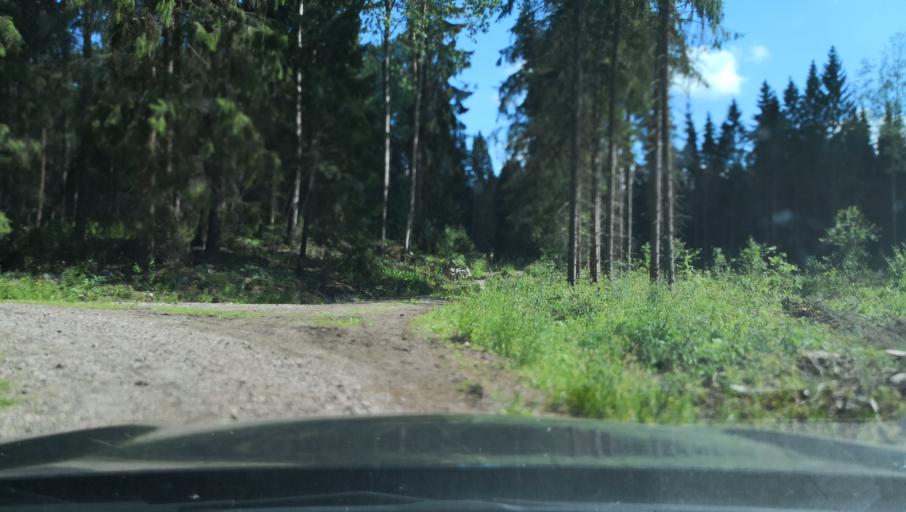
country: SE
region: Vaestmanland
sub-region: Kungsors Kommun
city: Kungsoer
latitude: 59.3399
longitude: 16.0624
